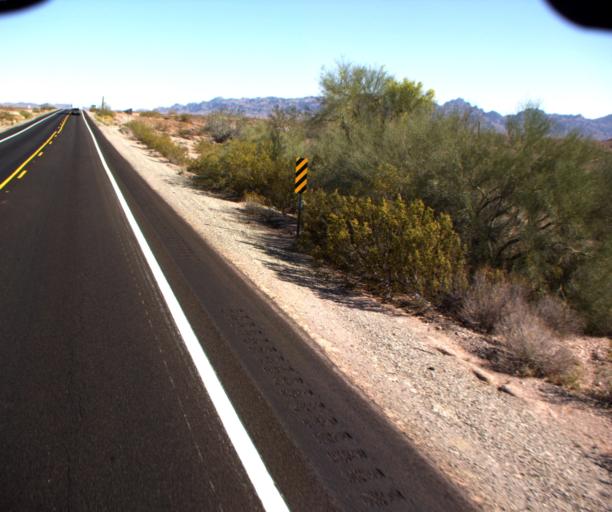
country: US
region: Arizona
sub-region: Yuma County
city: Wellton
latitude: 33.1146
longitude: -114.2940
